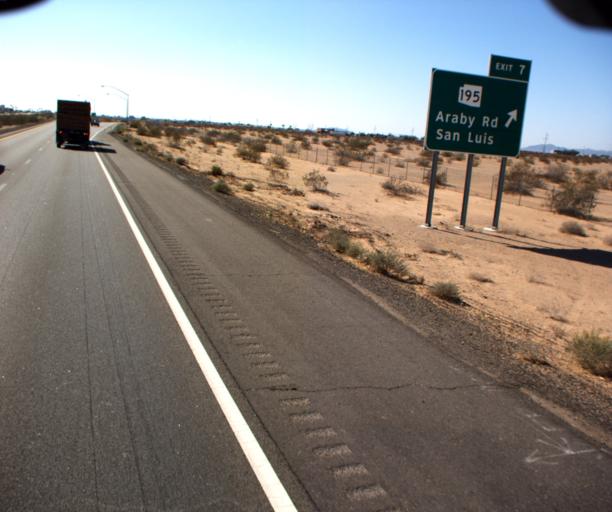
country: US
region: Arizona
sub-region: Yuma County
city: Fortuna Foothills
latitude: 32.6787
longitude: -114.5140
